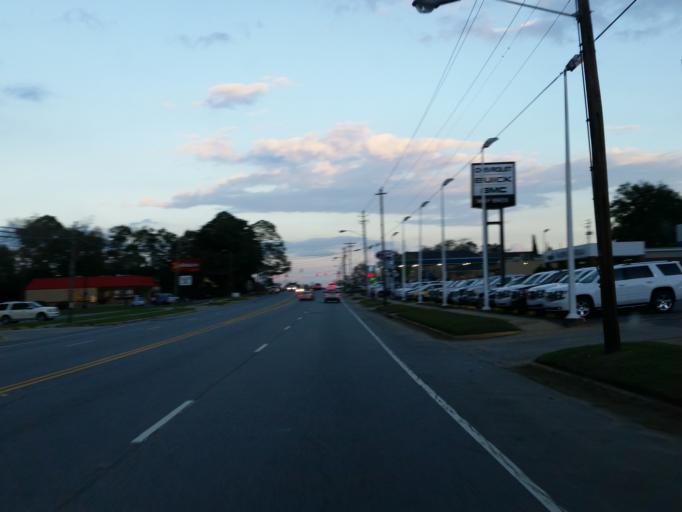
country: US
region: Georgia
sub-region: Pulaski County
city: Hawkinsville
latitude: 32.2813
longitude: -83.4760
